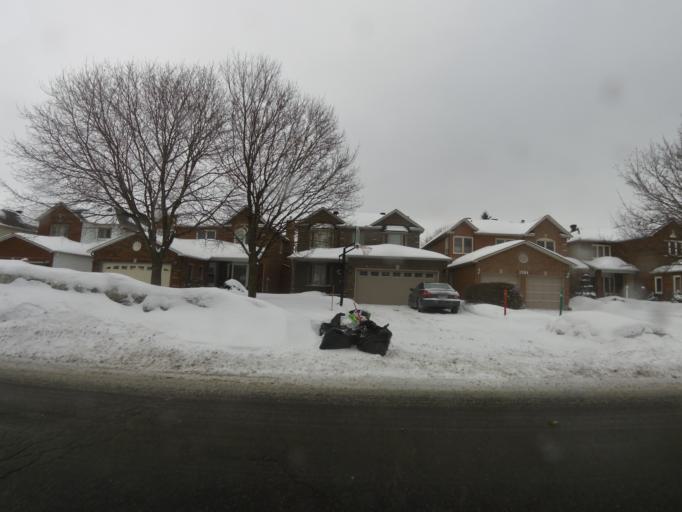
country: CA
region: Ontario
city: Ottawa
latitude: 45.3734
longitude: -75.6106
